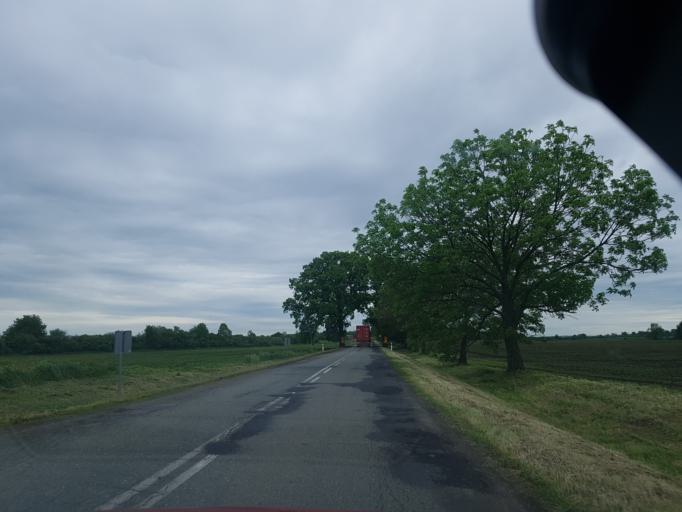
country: PL
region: Lower Silesian Voivodeship
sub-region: Powiat wroclawski
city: Kobierzyce
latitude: 50.9480
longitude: 16.9188
